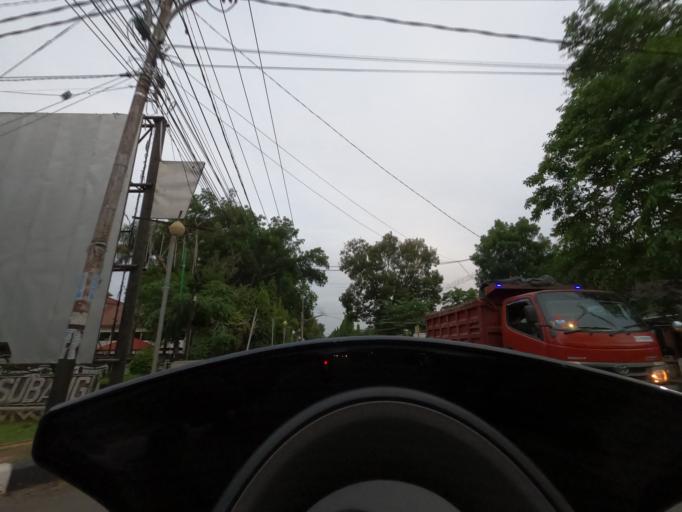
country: ID
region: West Java
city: Lembang
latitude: -6.5728
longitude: 107.7614
